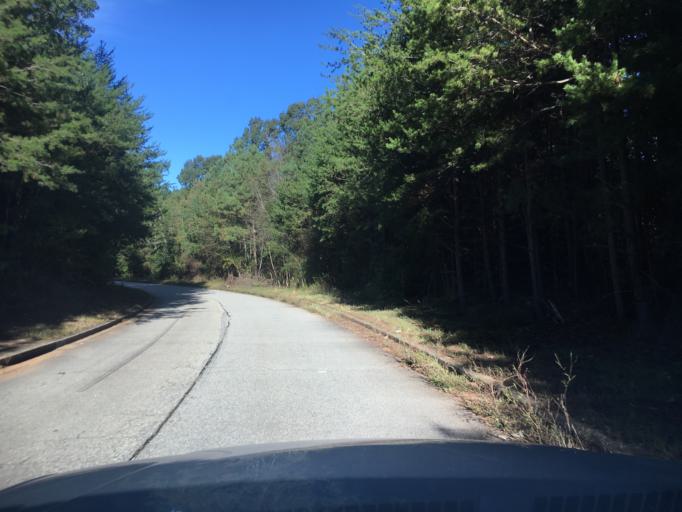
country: US
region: South Carolina
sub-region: Spartanburg County
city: Wellford
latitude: 34.9100
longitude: -82.0892
